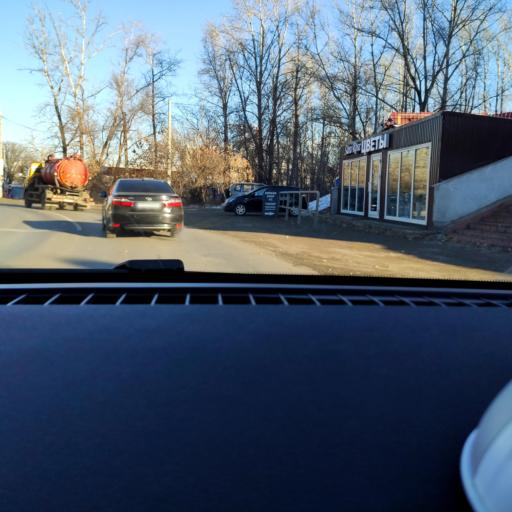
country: RU
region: Samara
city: Rozhdestveno
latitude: 53.1436
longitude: 50.0494
